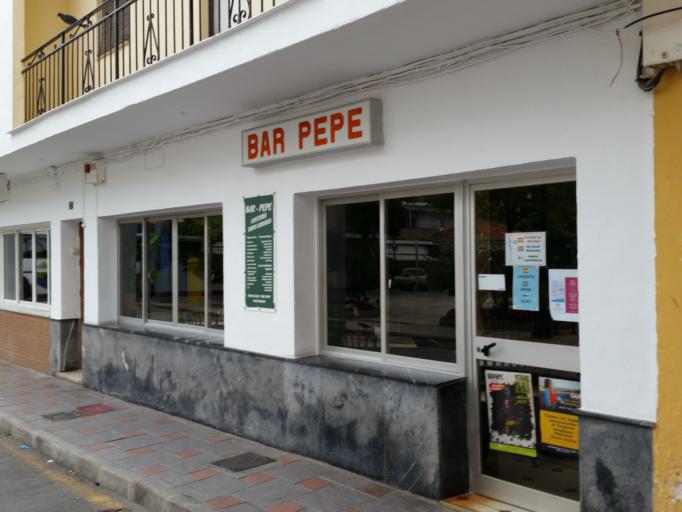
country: ES
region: Andalusia
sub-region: Provincia de Malaga
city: Fuengirola
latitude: 36.5529
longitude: -4.6153
